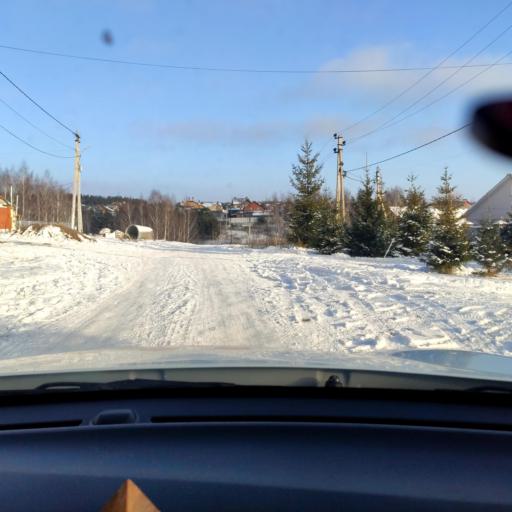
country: RU
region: Tatarstan
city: Vysokaya Gora
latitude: 55.8202
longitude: 49.2626
